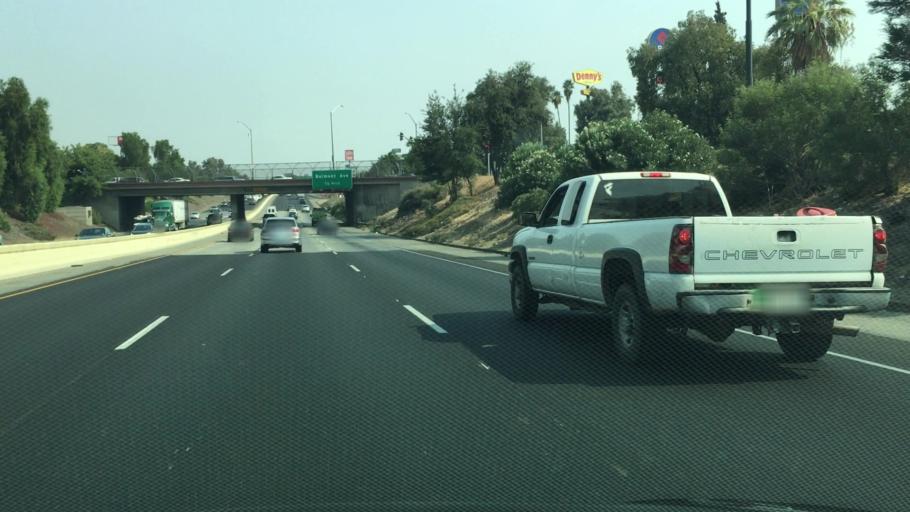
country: US
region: California
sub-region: Fresno County
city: West Park
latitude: 36.7585
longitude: -119.8305
